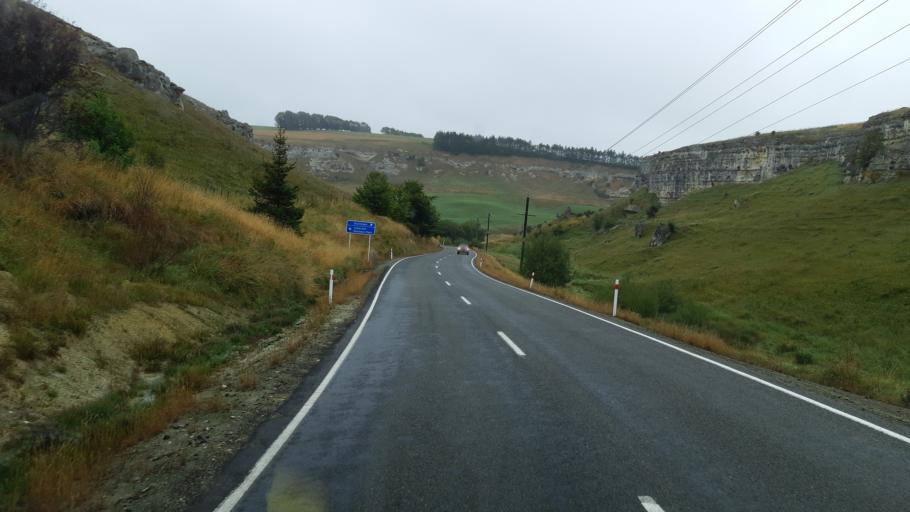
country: NZ
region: Otago
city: Oamaru
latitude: -44.9362
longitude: 170.6864
